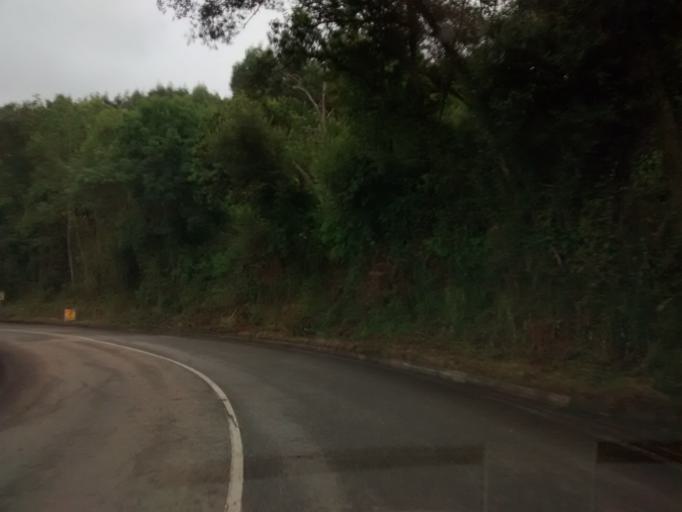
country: ES
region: Asturias
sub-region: Province of Asturias
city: Villaviciosa
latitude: 43.5330
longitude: -5.3966
